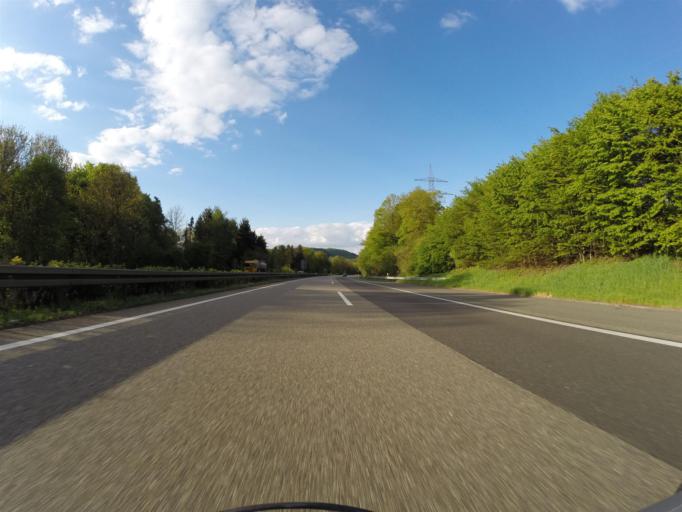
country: DE
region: Saarland
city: Sankt Ingbert
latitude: 49.2358
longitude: 7.0816
